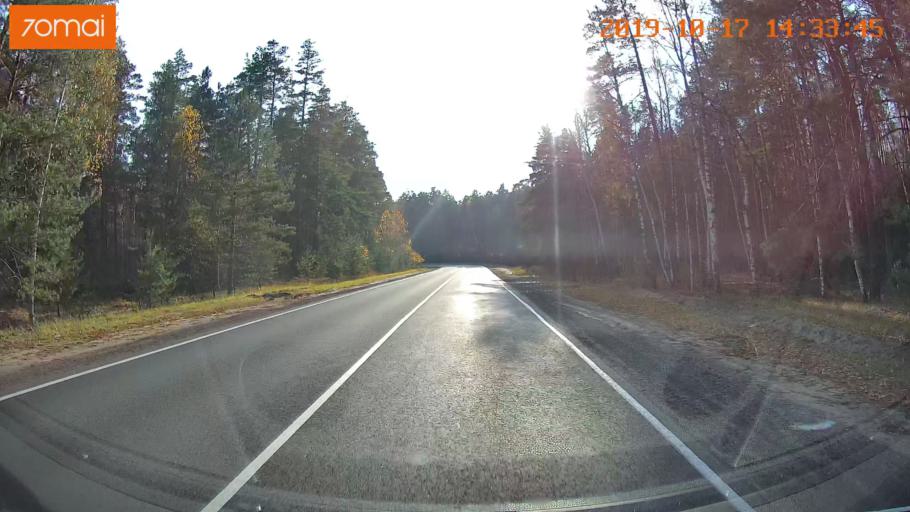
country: RU
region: Rjazan
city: Solotcha
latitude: 54.9201
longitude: 39.9972
